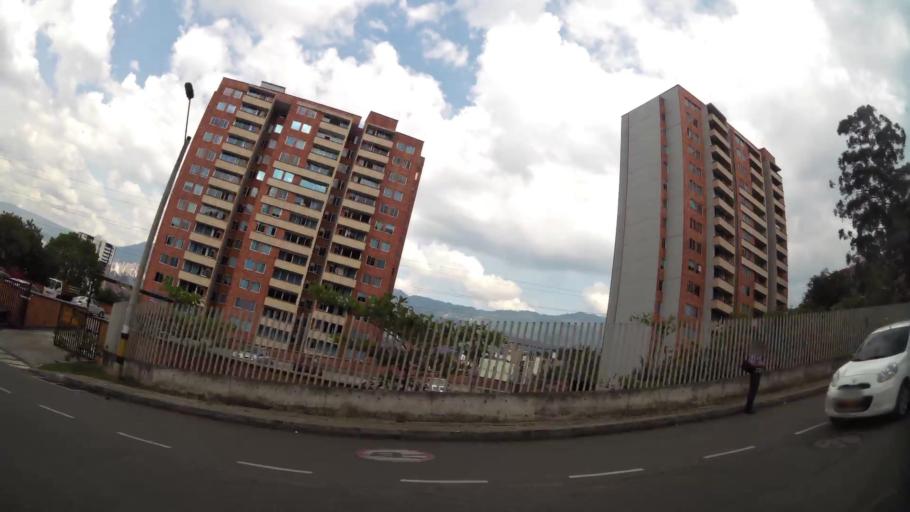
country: CO
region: Antioquia
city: Envigado
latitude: 6.1578
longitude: -75.5982
